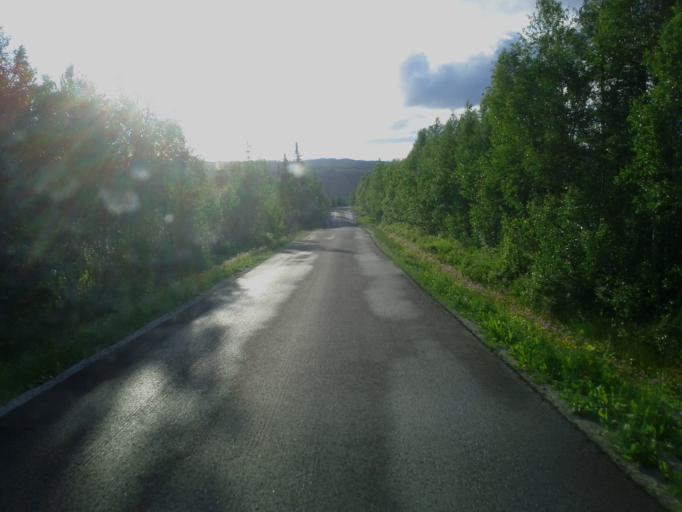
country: NO
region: Nordland
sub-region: Grane
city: Trofors
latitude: 65.4683
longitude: 13.6665
